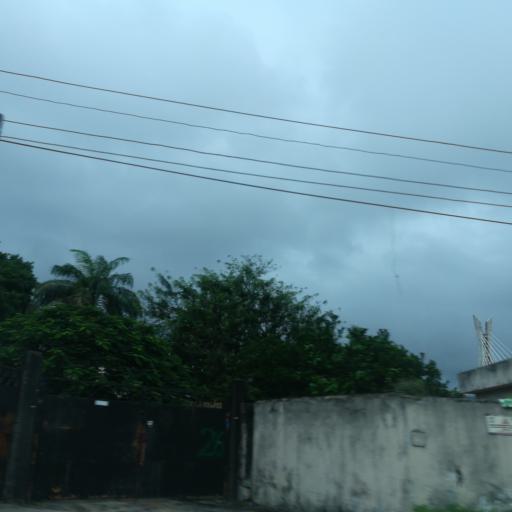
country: NG
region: Lagos
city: Ikoyi
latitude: 6.4510
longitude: 3.4493
